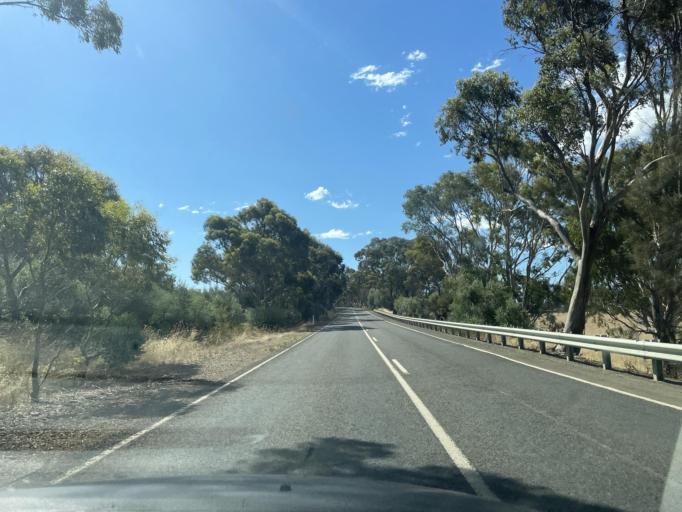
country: AU
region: South Australia
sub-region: Clare and Gilbert Valleys
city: Clare
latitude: -33.9054
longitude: 138.7114
